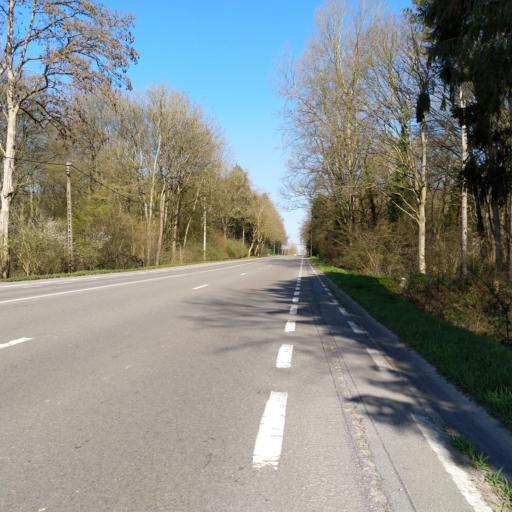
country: BE
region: Wallonia
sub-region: Province du Hainaut
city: Jurbise
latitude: 50.4961
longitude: 3.9372
